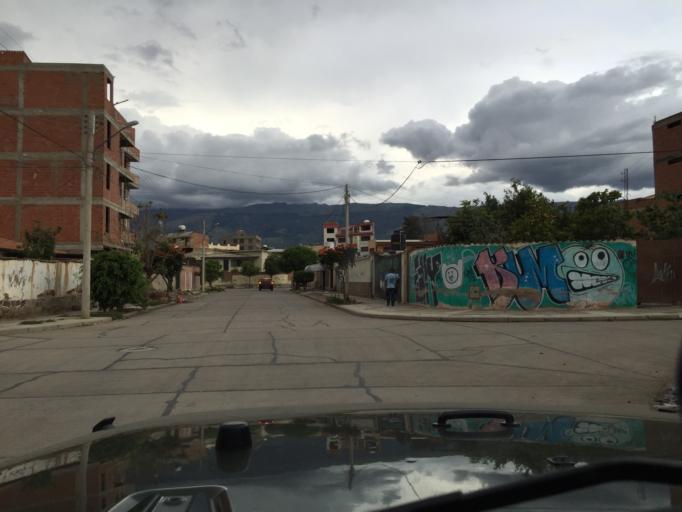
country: BO
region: Cochabamba
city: Cochabamba
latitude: -17.4183
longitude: -66.1613
